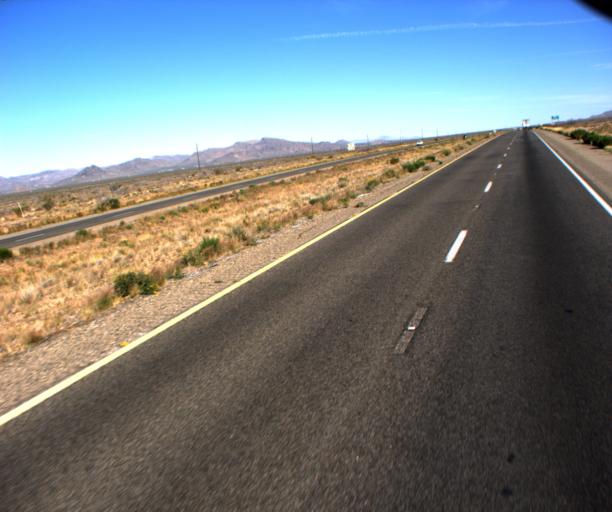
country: US
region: Arizona
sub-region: Mohave County
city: Golden Valley
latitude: 35.2870
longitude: -114.1796
